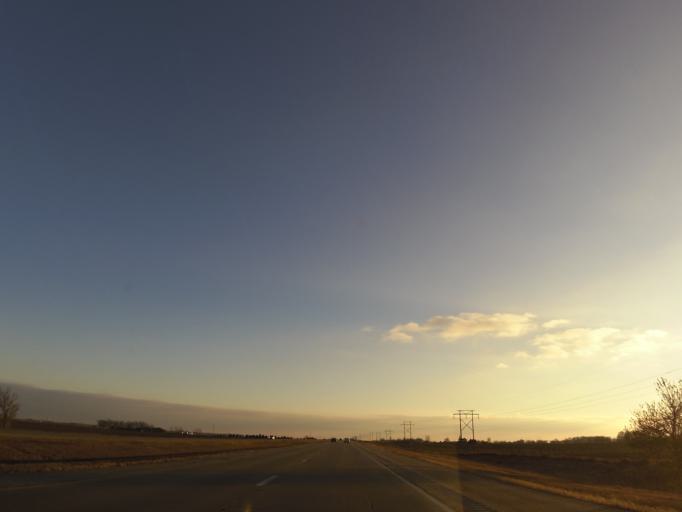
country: US
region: Illinois
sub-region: Woodford County
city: Minonk
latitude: 40.9473
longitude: -89.0567
